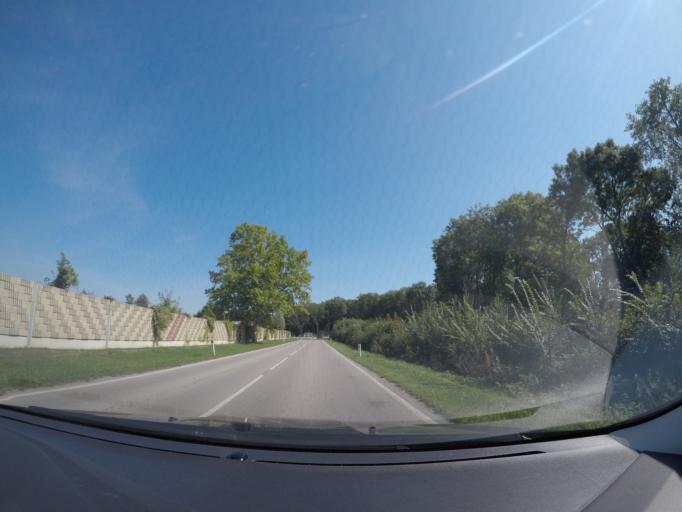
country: AT
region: Lower Austria
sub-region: Politischer Bezirk Baden
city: Seibersdorf
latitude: 47.9585
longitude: 16.5232
